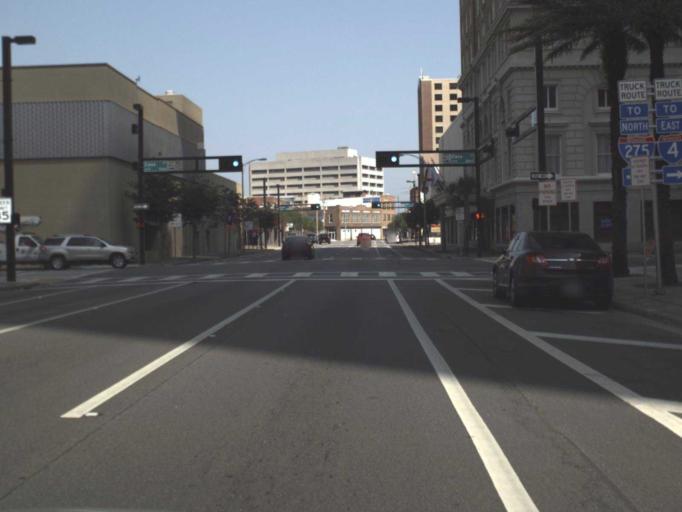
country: US
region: Florida
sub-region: Hillsborough County
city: Tampa
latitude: 27.9513
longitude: -82.4585
